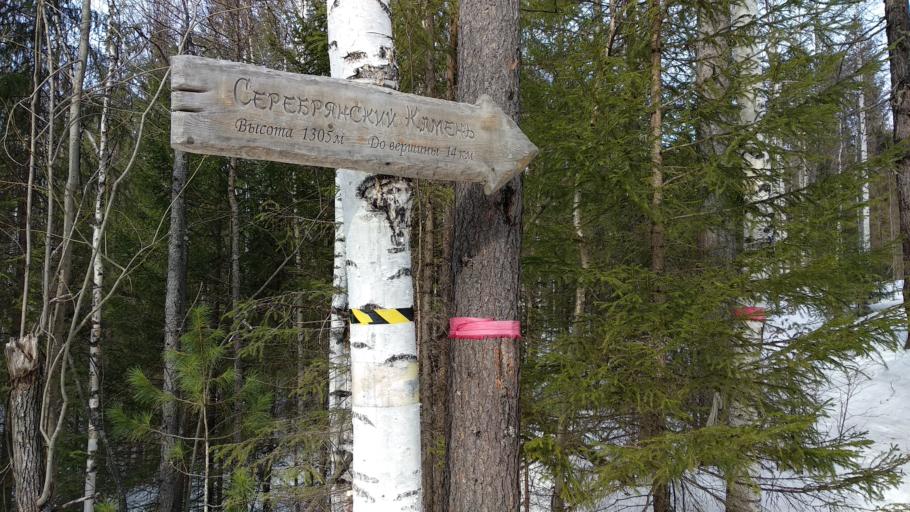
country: RU
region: Sverdlovsk
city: Karpinsk
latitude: 59.5626
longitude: 59.3530
